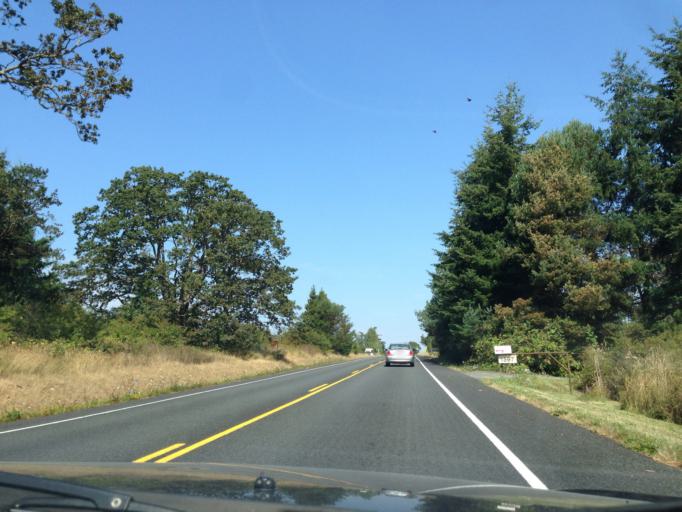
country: US
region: Washington
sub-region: San Juan County
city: Friday Harbor
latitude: 48.5067
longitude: -123.0361
